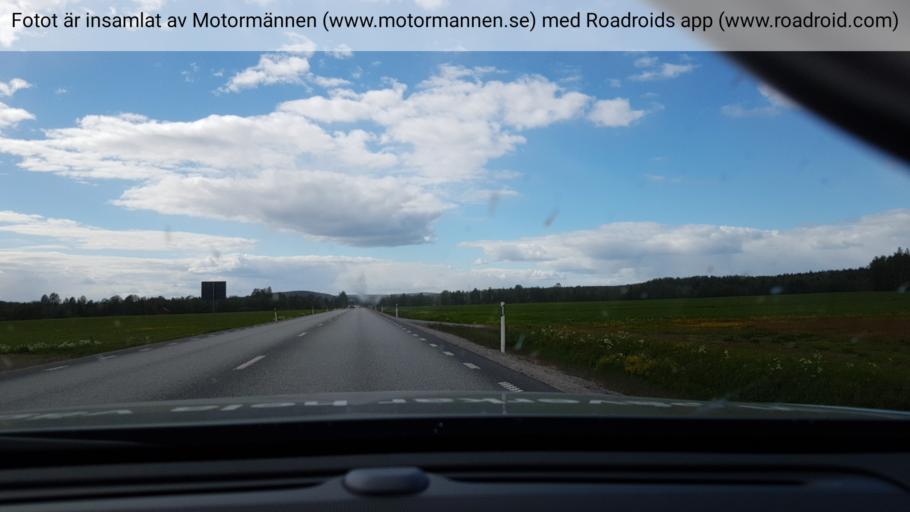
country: SE
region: Vaesterbotten
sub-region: Umea Kommun
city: Roback
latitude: 63.8686
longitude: 20.0784
